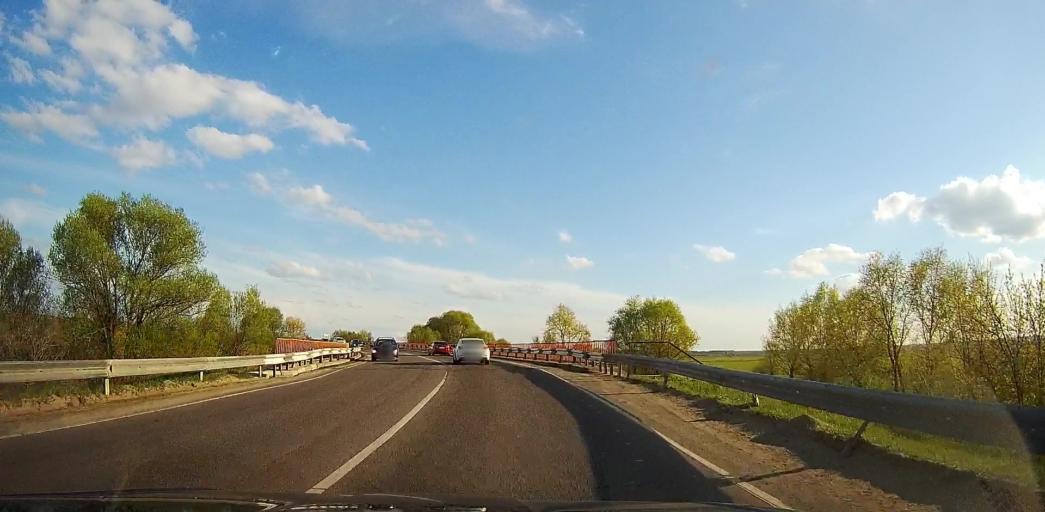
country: RU
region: Moskovskaya
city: Ramenskoye
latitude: 55.5157
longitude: 38.2749
